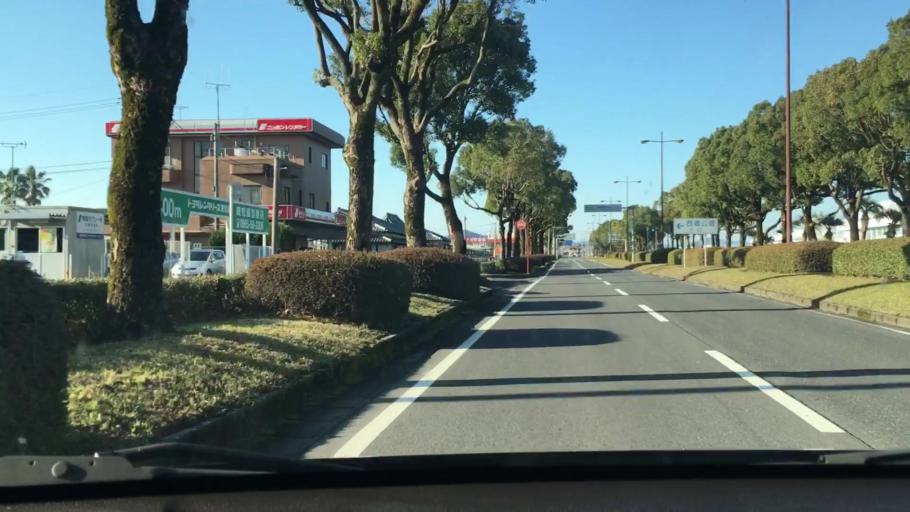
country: JP
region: Kagoshima
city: Kajiki
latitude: 31.7977
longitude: 130.7166
